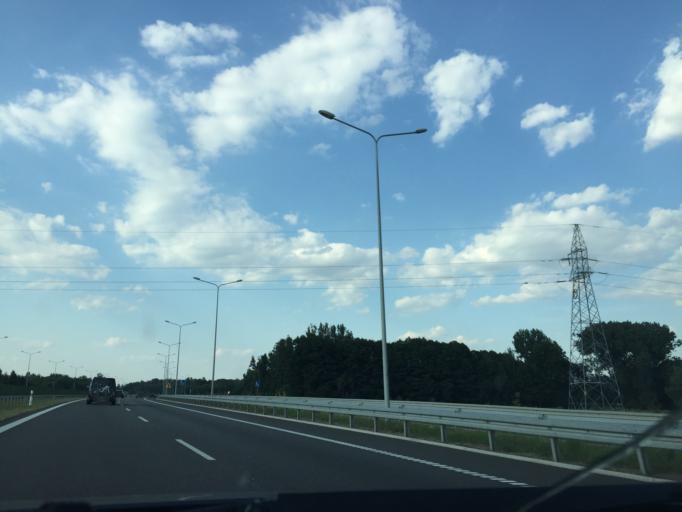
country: PL
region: Masovian Voivodeship
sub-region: Powiat szydlowiecki
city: Oronsko
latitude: 51.3376
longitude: 21.0148
